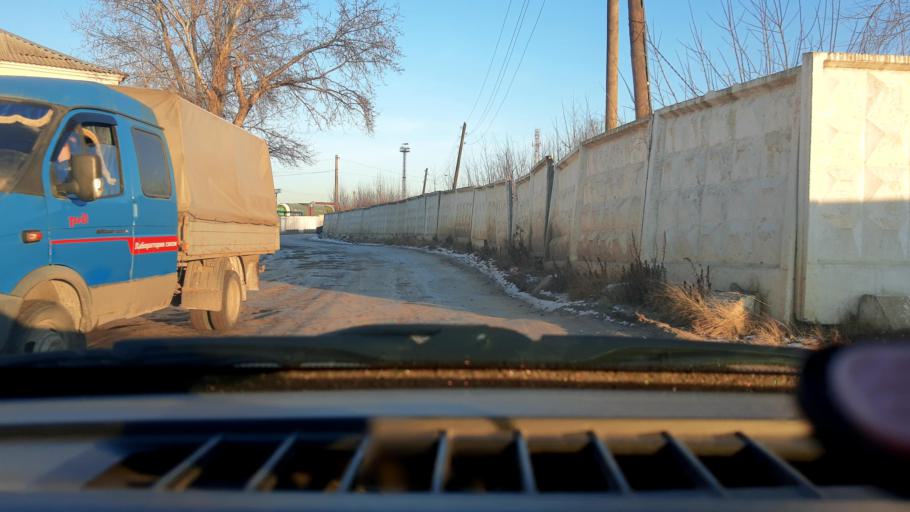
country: RU
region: Nizjnij Novgorod
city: Gorbatovka
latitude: 56.2774
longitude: 43.8399
